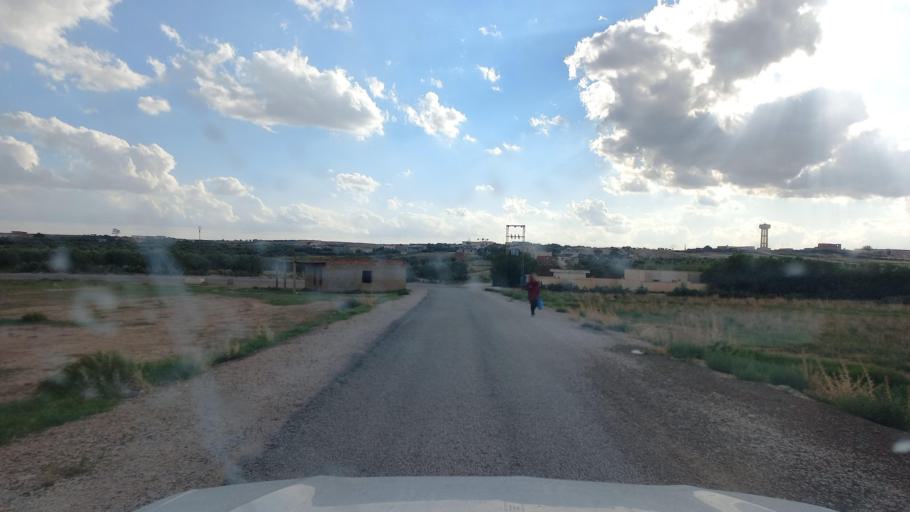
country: TN
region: Al Qasrayn
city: Sbiba
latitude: 35.3744
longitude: 9.0700
